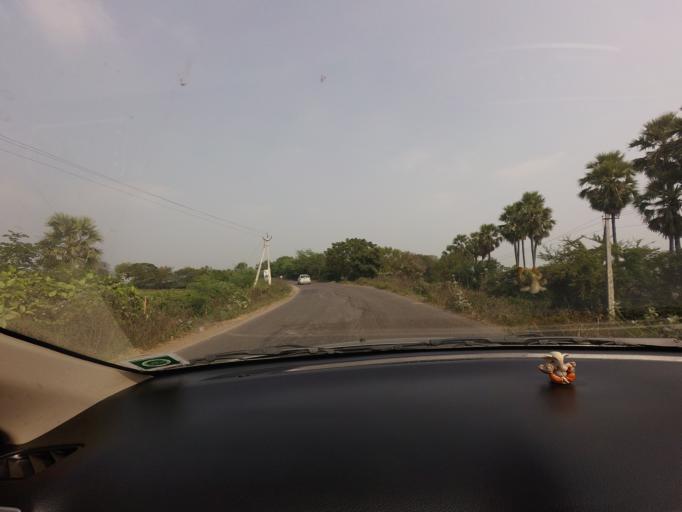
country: IN
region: Andhra Pradesh
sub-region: Krishna
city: Kankipadu
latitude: 16.4544
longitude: 80.7934
